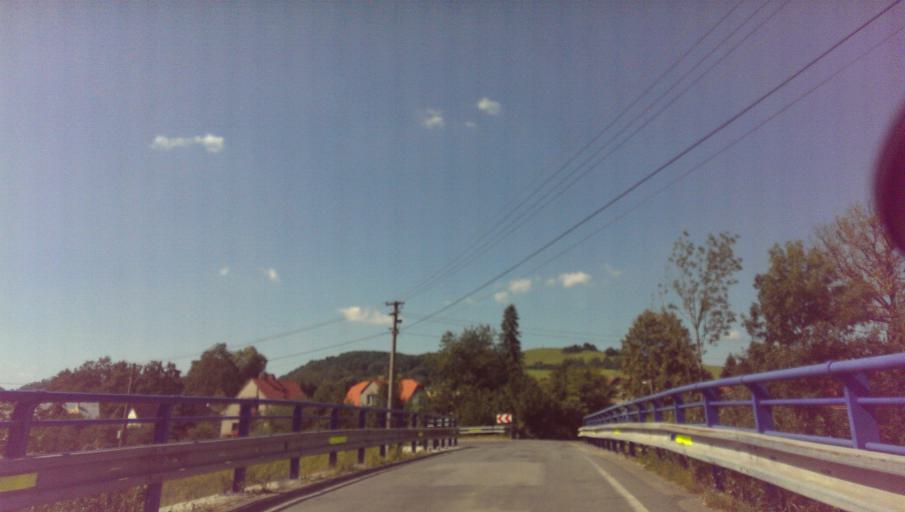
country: CZ
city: Hukvaldy
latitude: 49.6366
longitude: 18.2172
